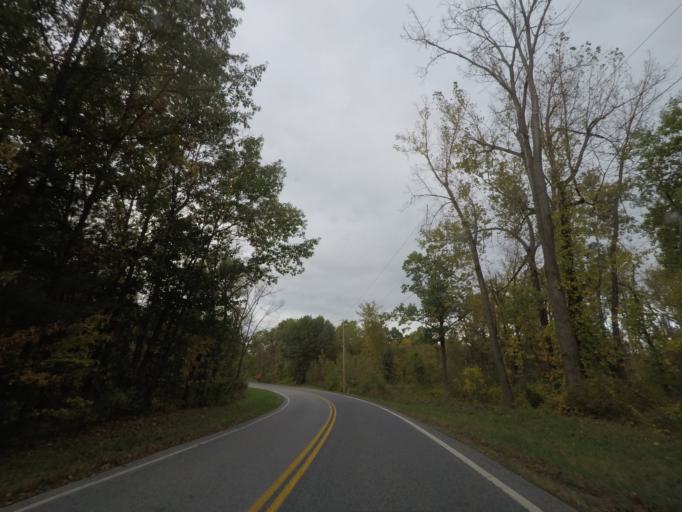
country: US
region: New York
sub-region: Saratoga County
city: Mechanicville
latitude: 42.8794
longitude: -73.7323
